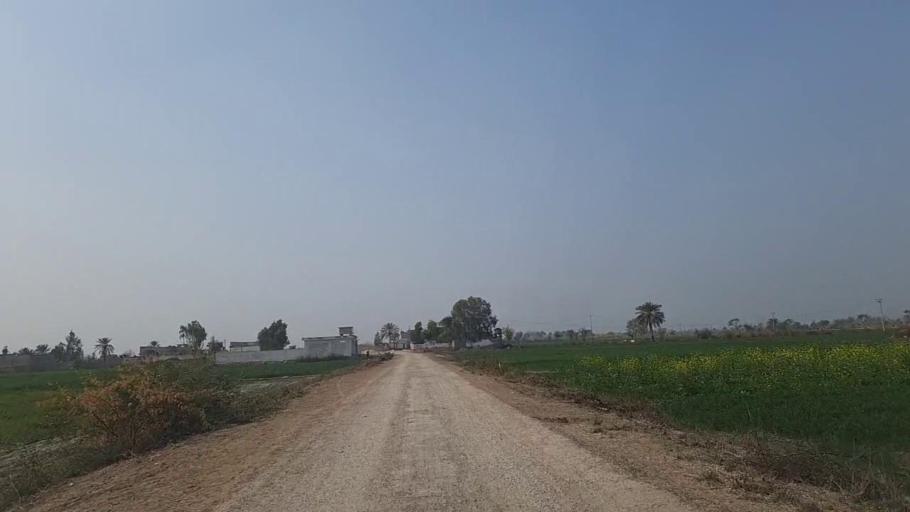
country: PK
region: Sindh
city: Daur
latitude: 26.4488
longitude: 68.4449
